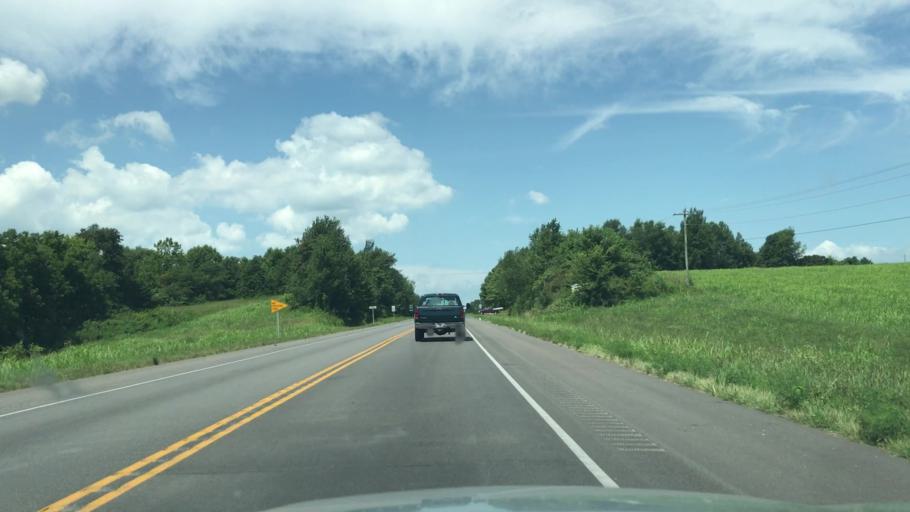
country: US
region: Kentucky
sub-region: Clinton County
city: Albany
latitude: 36.7535
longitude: -85.1200
